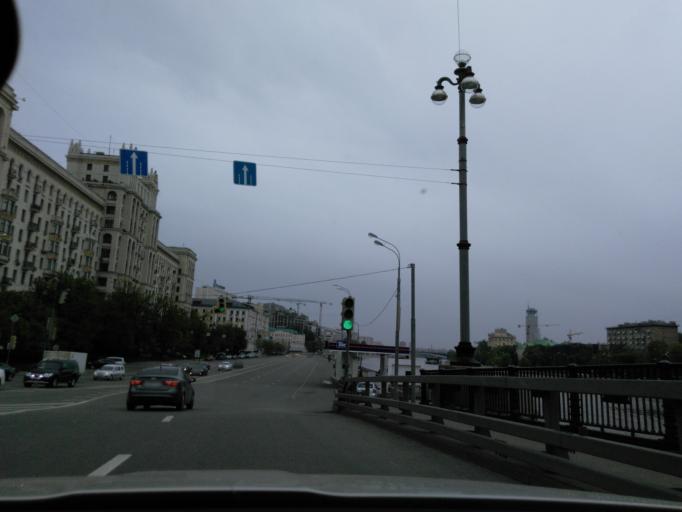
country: RU
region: Moscow
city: Zamoskvorech'ye
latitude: 55.7470
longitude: 37.6404
